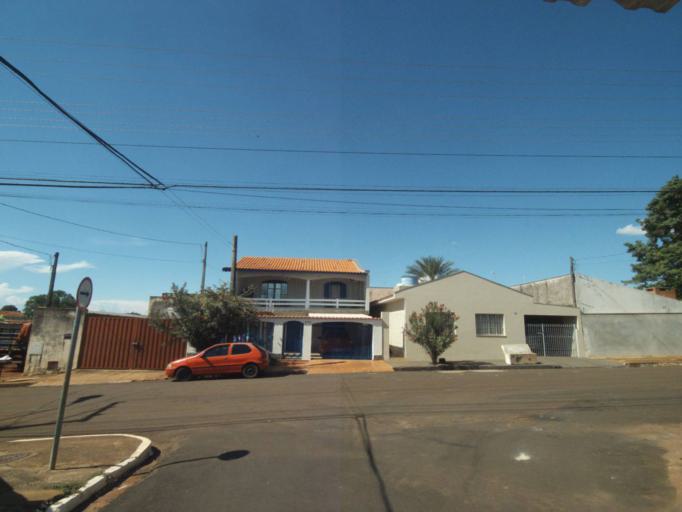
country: BR
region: Parana
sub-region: Sertanopolis
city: Sertanopolis
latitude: -23.0369
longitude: -50.8184
